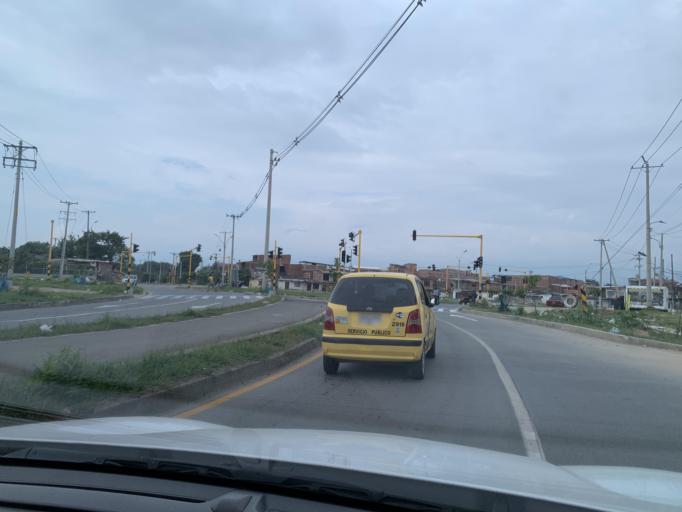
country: CO
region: Valle del Cauca
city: Cali
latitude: 3.4151
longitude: -76.4825
